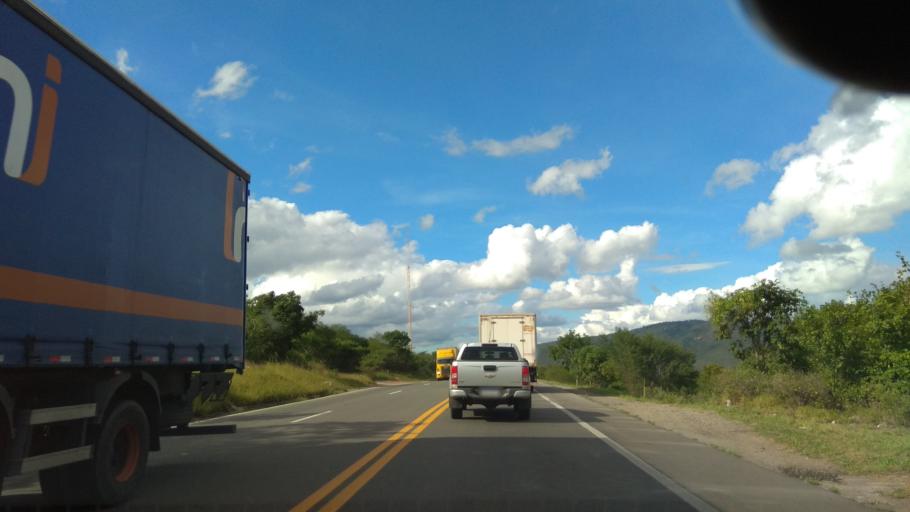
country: BR
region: Bahia
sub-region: Castro Alves
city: Castro Alves
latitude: -12.6555
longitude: -39.6186
